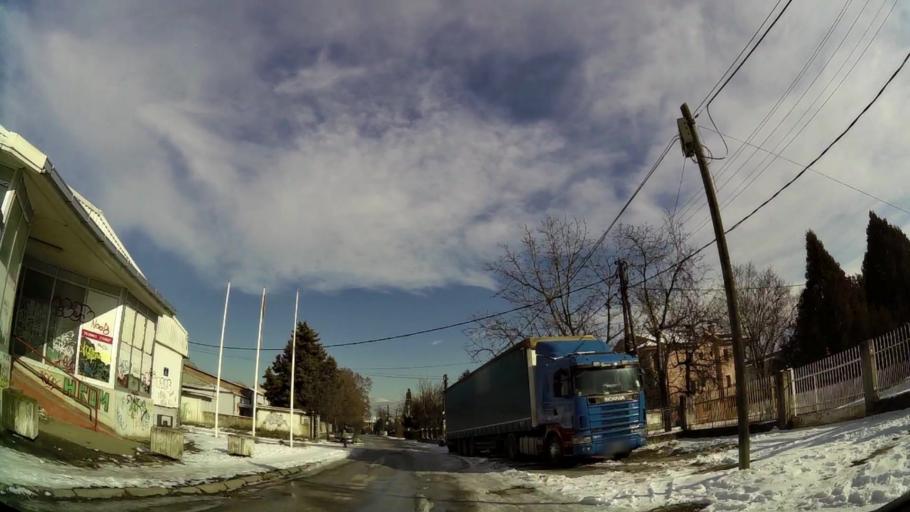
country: MK
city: Krushopek
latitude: 42.0004
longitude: 21.3726
